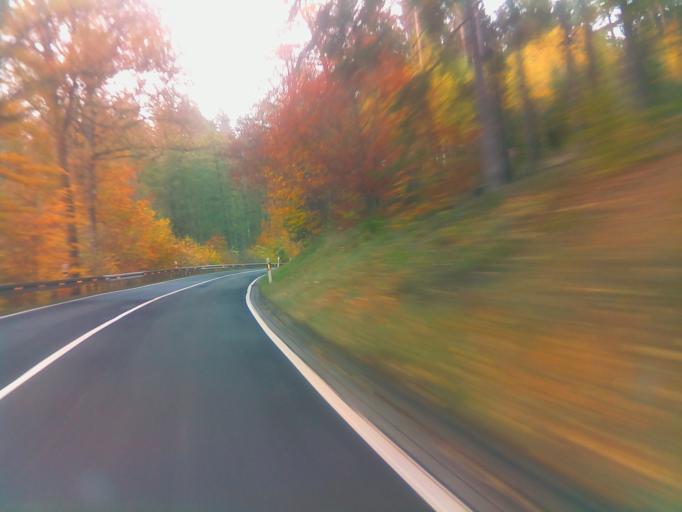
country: DE
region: Thuringia
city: Urnshausen
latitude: 50.7587
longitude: 10.1796
